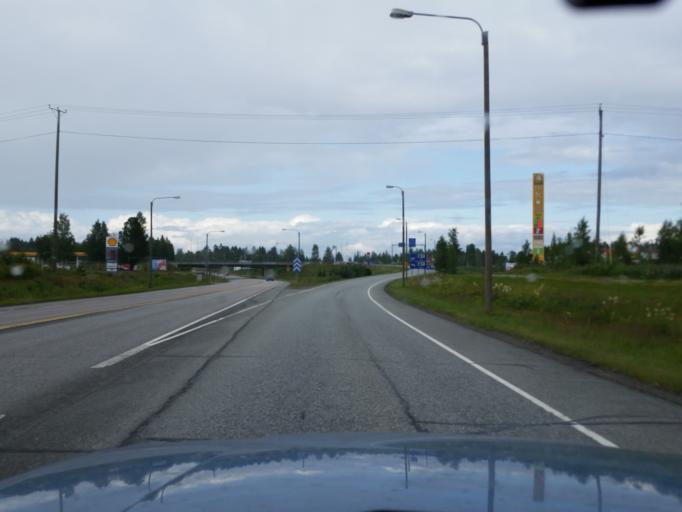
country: FI
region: Southern Savonia
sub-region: Pieksaemaeki
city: Juva
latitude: 61.8960
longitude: 27.8014
